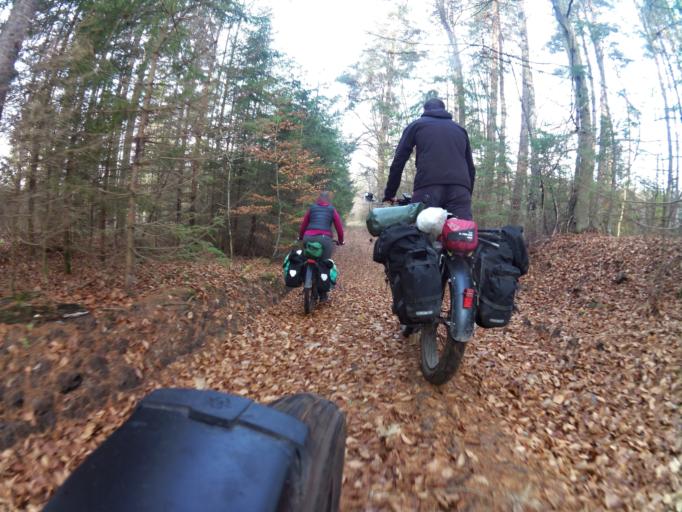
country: PL
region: West Pomeranian Voivodeship
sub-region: Powiat koszalinski
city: Polanow
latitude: 54.1854
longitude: 16.7212
